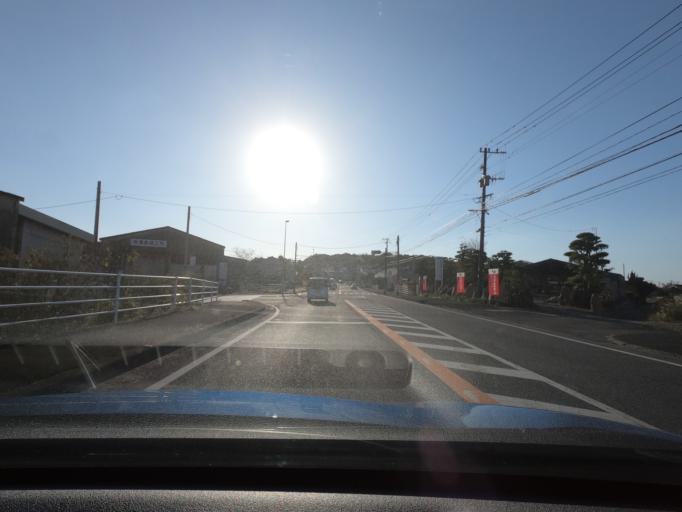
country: JP
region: Kagoshima
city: Akune
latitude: 32.0606
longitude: 130.2244
